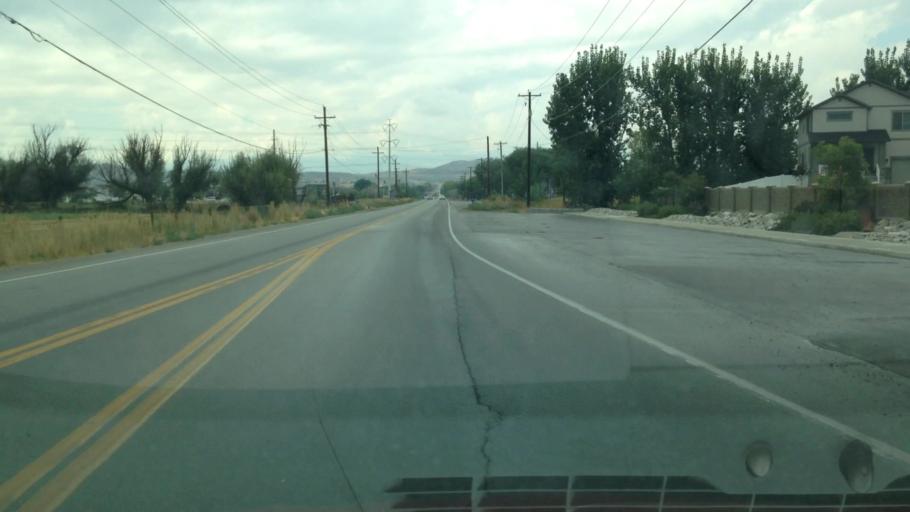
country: US
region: Utah
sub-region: Utah County
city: Lehi
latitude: 40.3873
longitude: -111.8872
